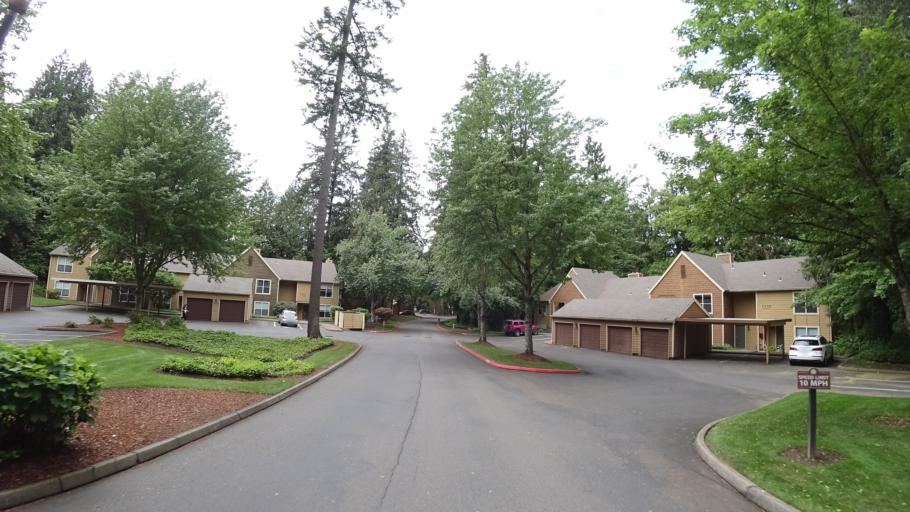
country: US
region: Oregon
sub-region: Washington County
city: Garden Home-Whitford
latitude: 45.4687
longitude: -122.7527
